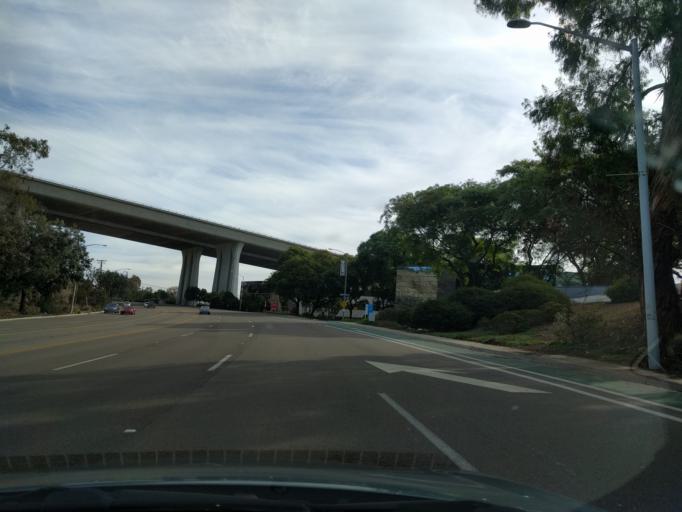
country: US
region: California
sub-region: San Diego County
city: San Diego
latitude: 32.7777
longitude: -117.1388
